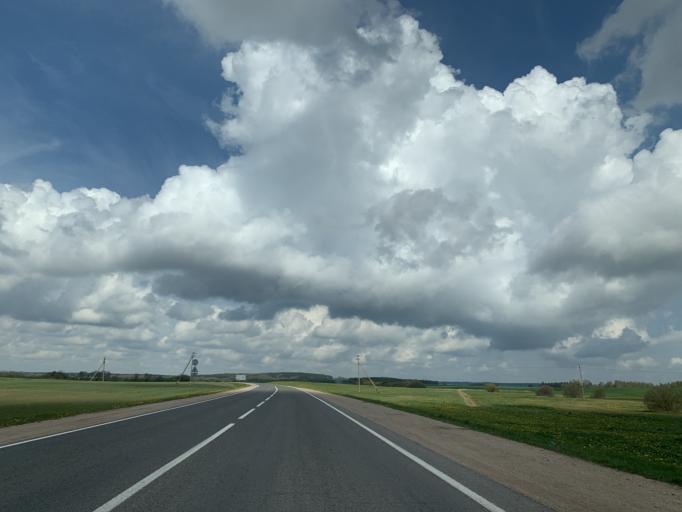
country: BY
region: Minsk
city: Nyasvizh
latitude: 53.2297
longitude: 26.7236
